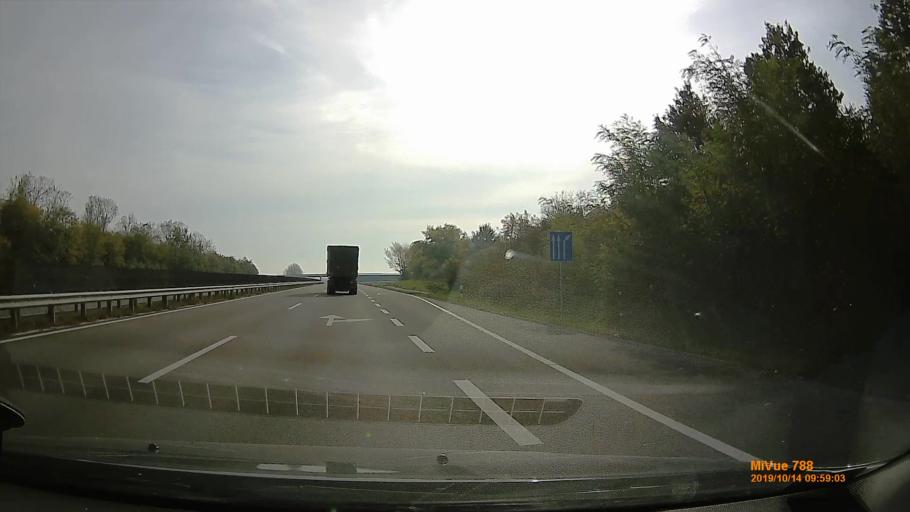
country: HU
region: Pest
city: Cegledbercel
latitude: 47.2239
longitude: 19.6893
